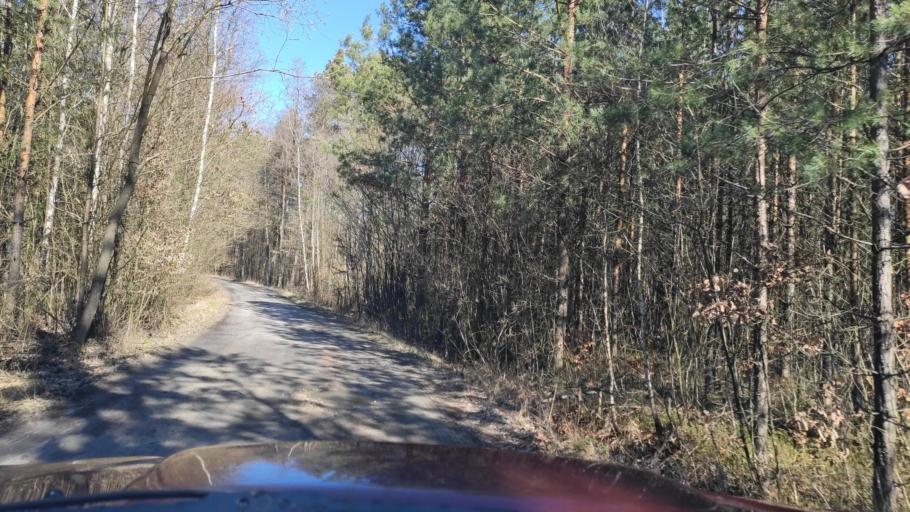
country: PL
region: Masovian Voivodeship
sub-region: Powiat kozienicki
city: Garbatka-Letnisko
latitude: 51.4426
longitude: 21.5364
